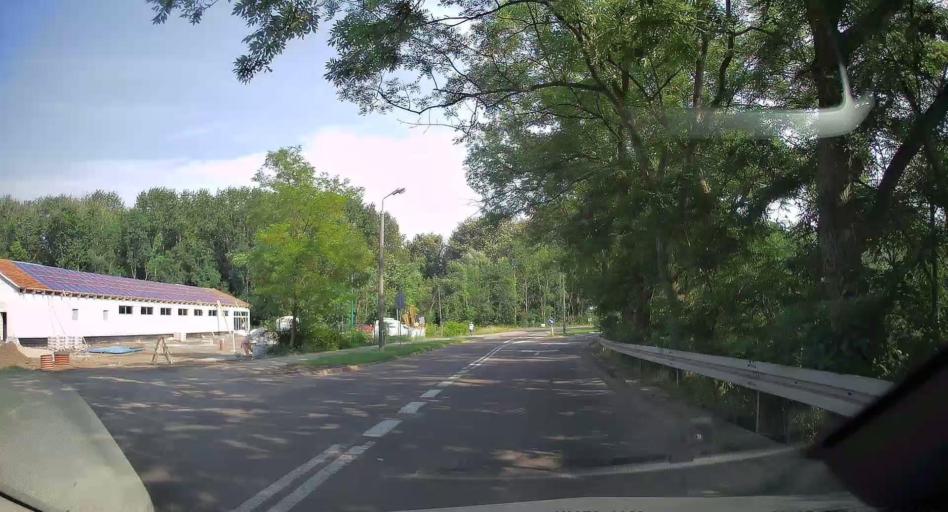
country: PL
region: Silesian Voivodeship
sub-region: Swietochlowice
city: Swietochlowice
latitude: 50.3087
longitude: 18.9208
